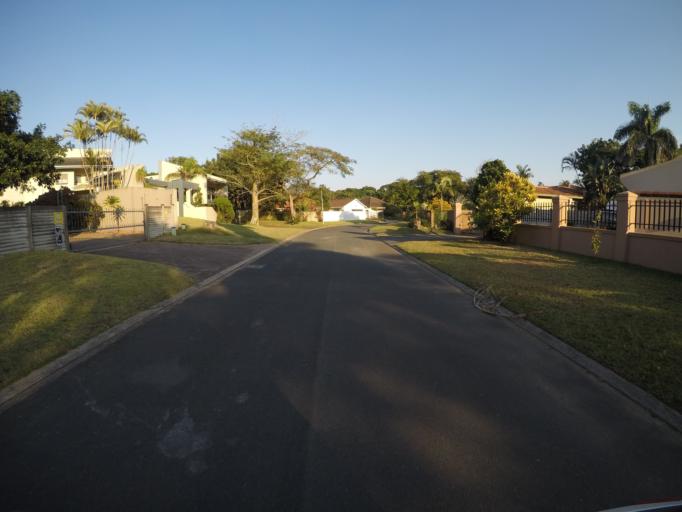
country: ZA
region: KwaZulu-Natal
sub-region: uThungulu District Municipality
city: Richards Bay
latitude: -28.7778
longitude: 32.1144
